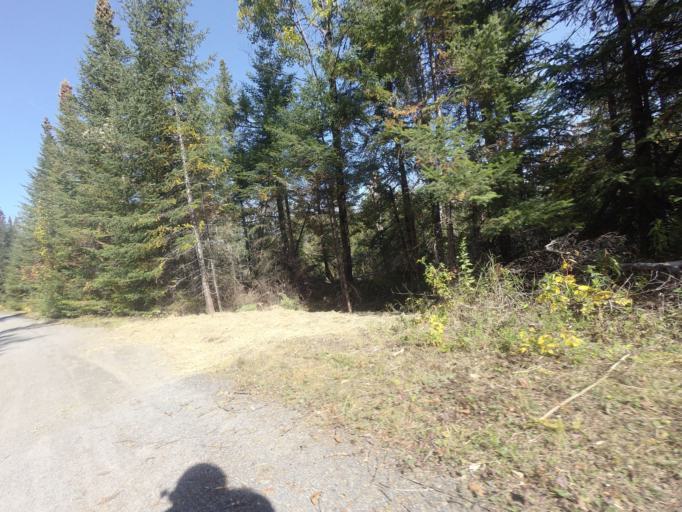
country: CA
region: Quebec
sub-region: Laurentides
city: Sainte-Agathe-des-Monts
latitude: 46.0870
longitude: -74.3410
